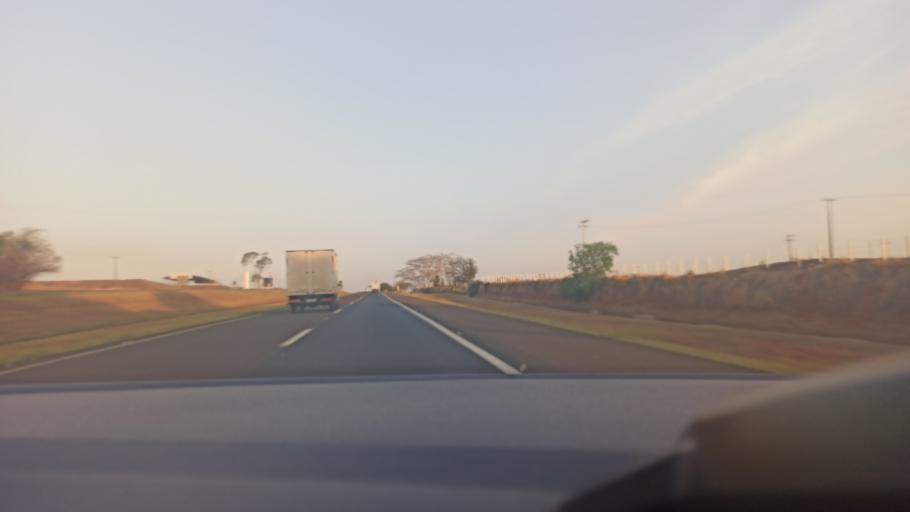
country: BR
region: Sao Paulo
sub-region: Santa Adelia
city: Santa Adelia
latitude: -21.3745
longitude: -48.7445
